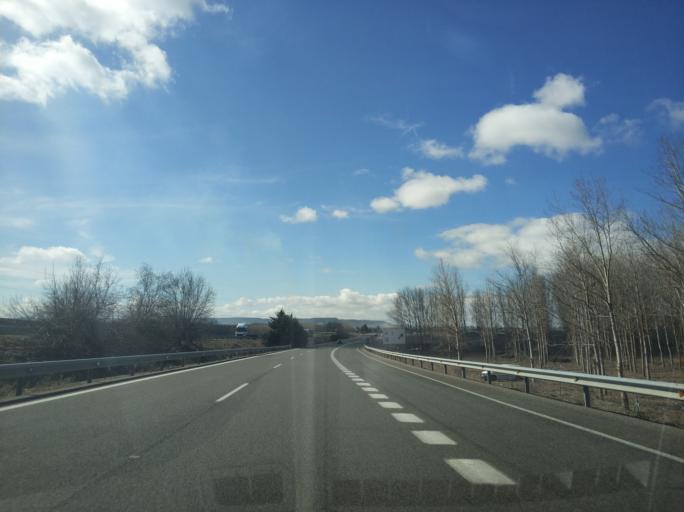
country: ES
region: Castille and Leon
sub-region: Provincia de Burgos
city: Villaverde-Mogina
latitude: 42.1629
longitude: -4.0759
